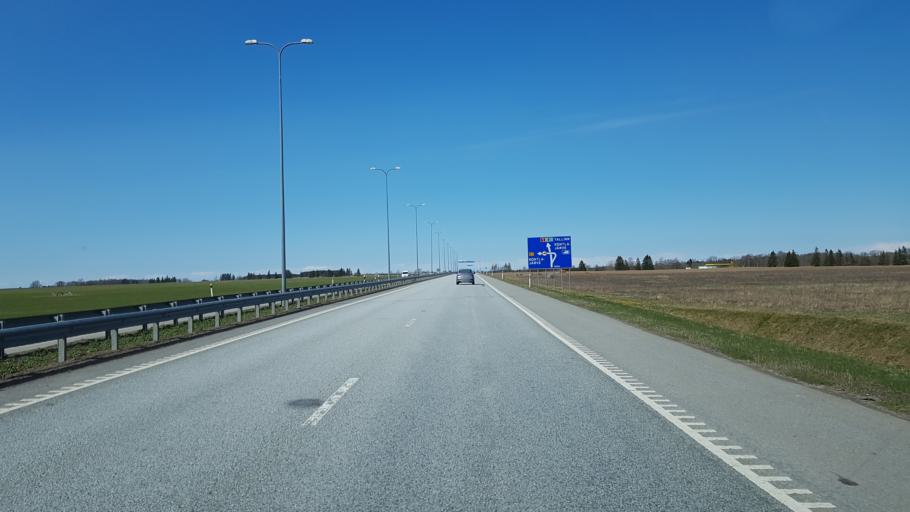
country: EE
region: Ida-Virumaa
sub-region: Kohtla-Jaerve linn
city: Kohtla-Jarve
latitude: 59.3928
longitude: 27.3372
